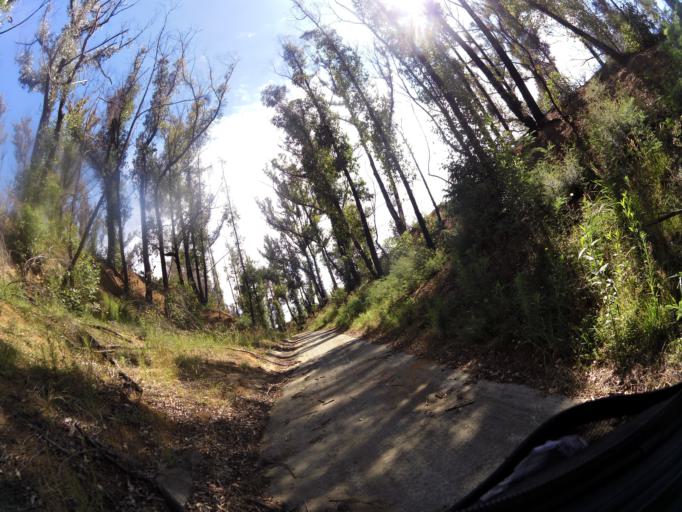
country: AU
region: Victoria
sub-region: East Gippsland
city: Lakes Entrance
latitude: -37.7309
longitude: 148.1625
